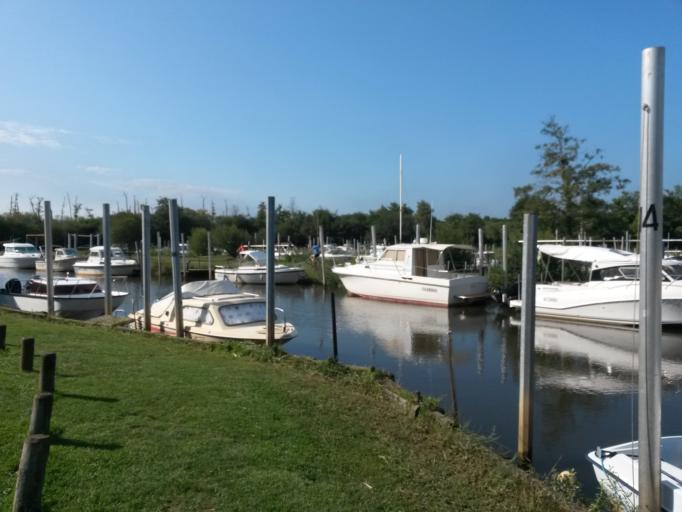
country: FR
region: Aquitaine
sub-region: Departement de la Gironde
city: Biganos
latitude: 44.6432
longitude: -0.9984
